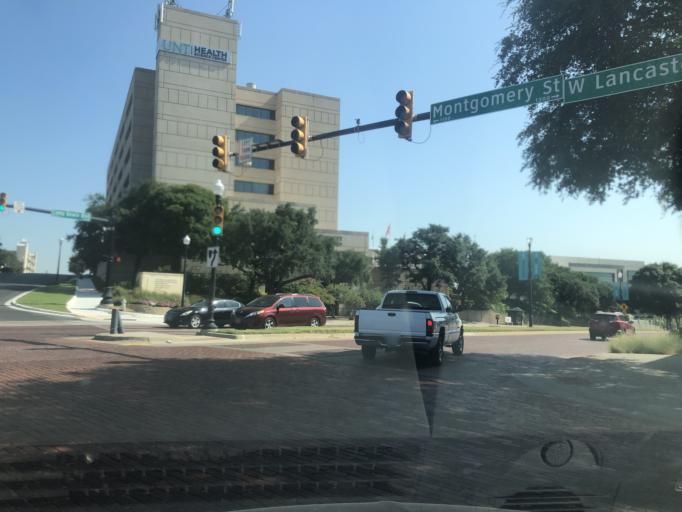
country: US
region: Texas
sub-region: Tarrant County
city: River Oaks
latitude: 32.7476
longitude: -97.3699
